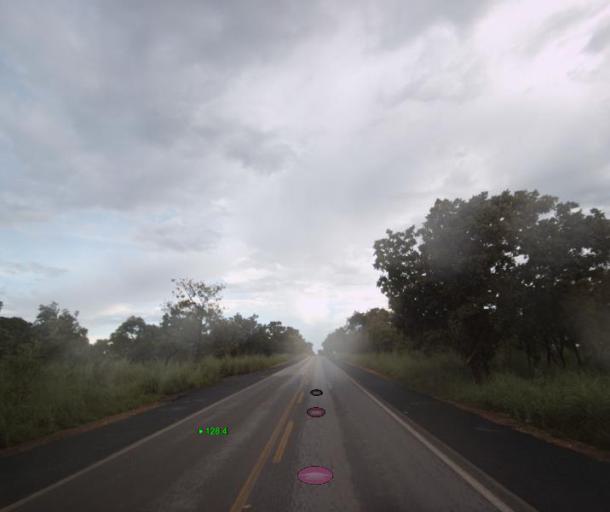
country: BR
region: Goias
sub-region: Porangatu
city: Porangatu
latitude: -13.8997
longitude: -49.0603
